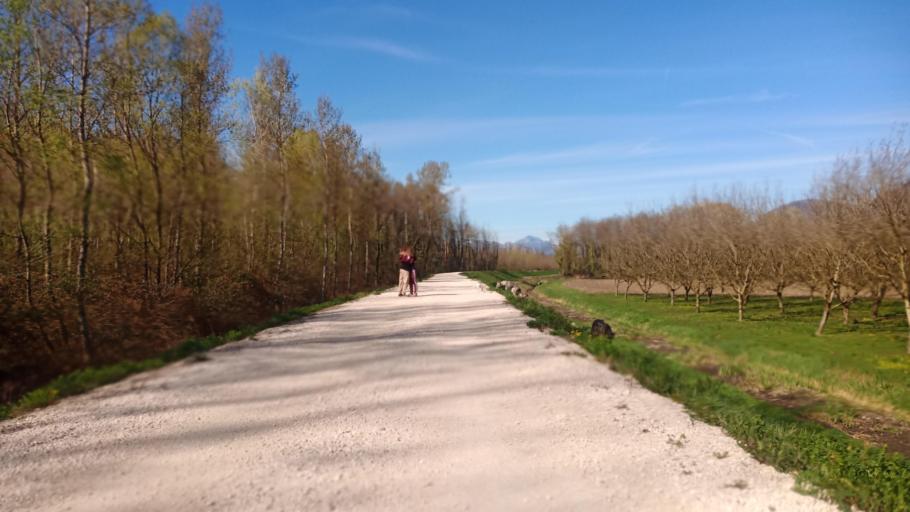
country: FR
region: Rhone-Alpes
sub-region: Departement de l'Isere
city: Tencin
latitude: 45.3105
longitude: 5.9426
